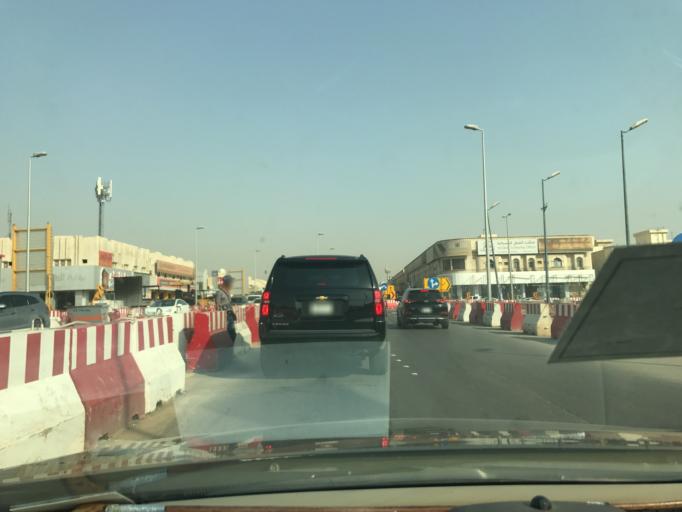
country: SA
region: Ar Riyad
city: Riyadh
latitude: 24.7538
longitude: 46.7696
